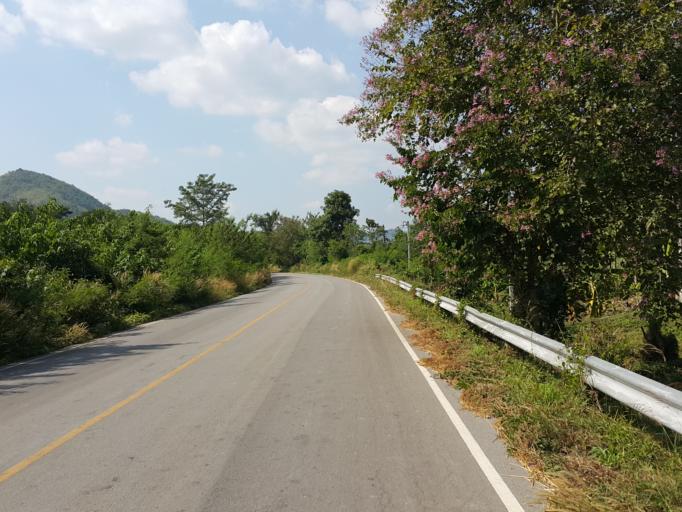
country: TH
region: Sukhothai
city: Thung Saliam
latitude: 17.3420
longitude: 99.4702
